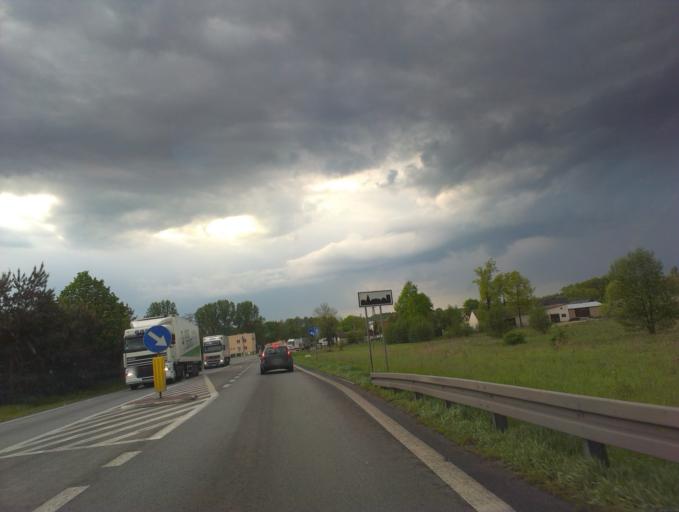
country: PL
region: Masovian Voivodeship
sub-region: Powiat grojecki
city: Pniewy
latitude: 51.8944
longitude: 20.7851
